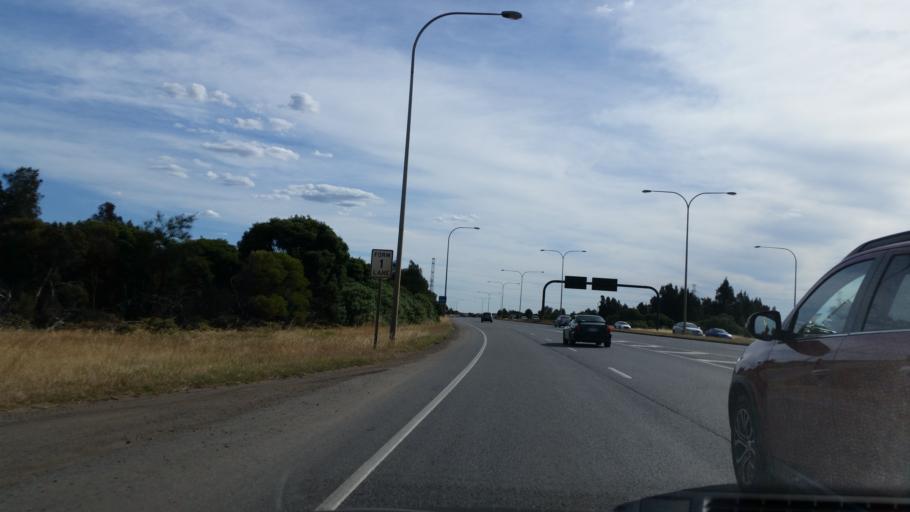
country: AU
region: South Australia
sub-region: Port Adelaide Enfield
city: Enfield
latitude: -34.8138
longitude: 138.5958
